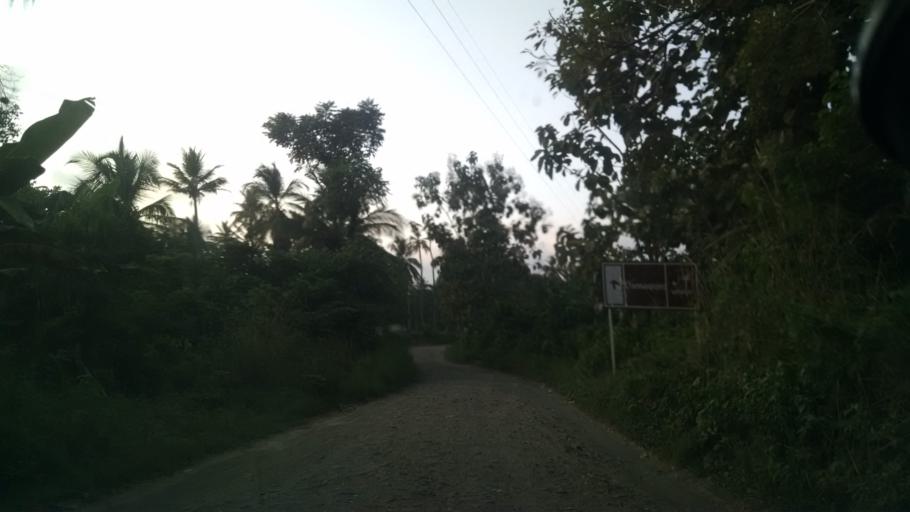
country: CO
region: Antioquia
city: San Juan de Uraba
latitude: 8.7219
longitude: -76.6021
